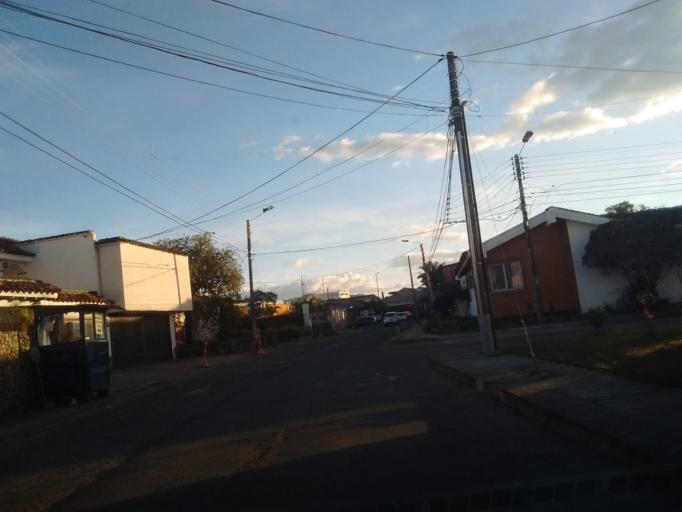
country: CO
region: Cauca
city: Popayan
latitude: 2.4582
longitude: -76.5966
